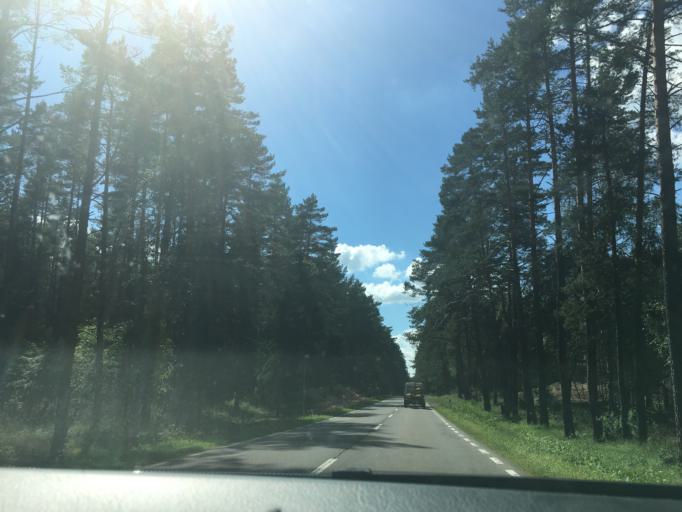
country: PL
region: Podlasie
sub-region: Powiat augustowski
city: Augustow
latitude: 53.8553
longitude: 23.0672
